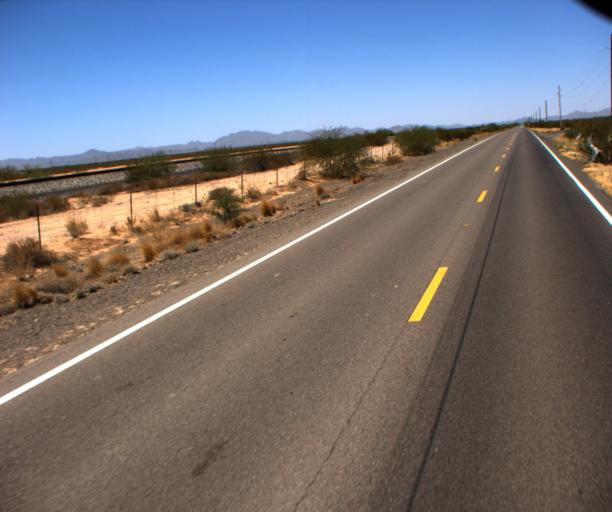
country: US
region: Arizona
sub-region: Pinal County
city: Maricopa
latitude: 33.0636
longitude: -112.2394
